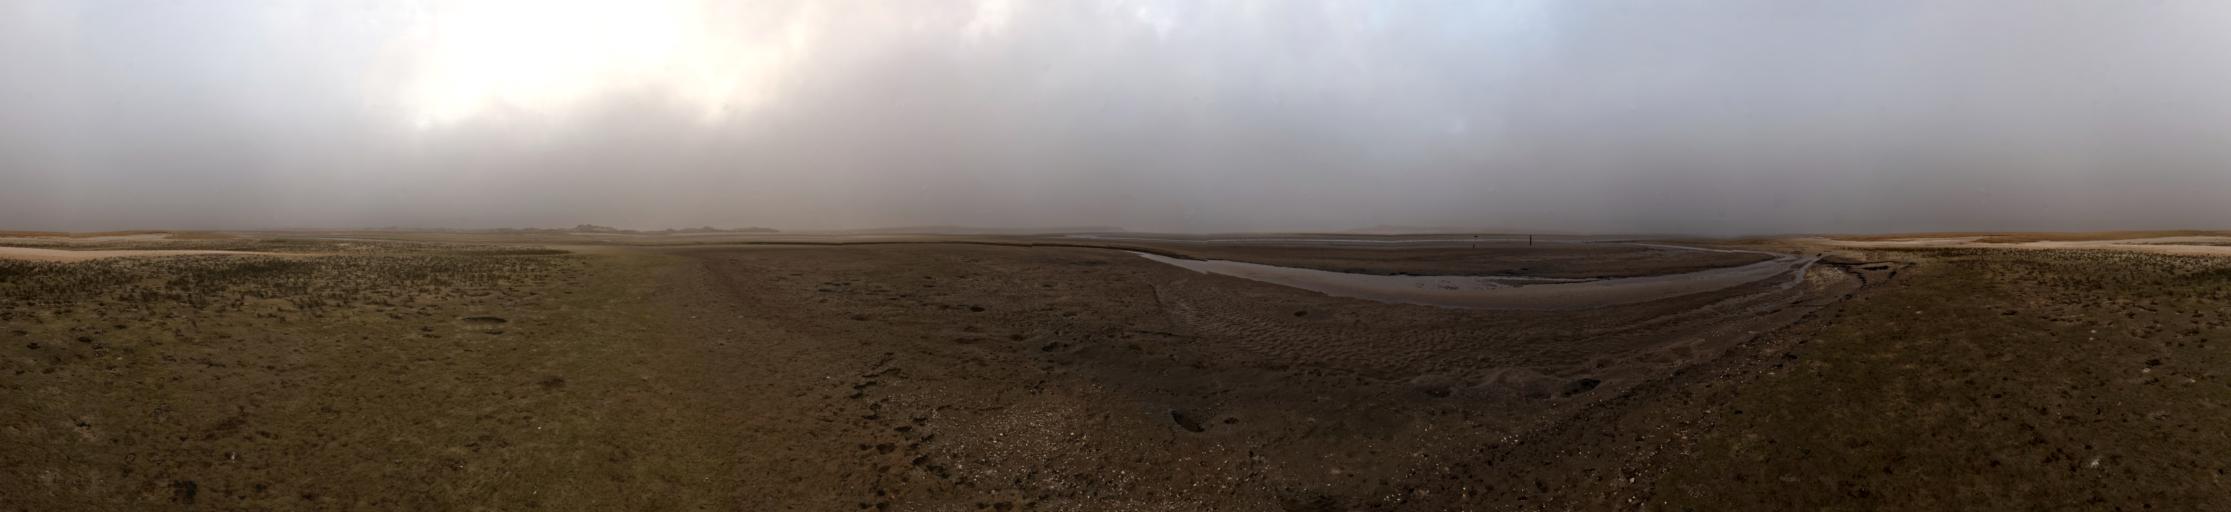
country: NL
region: North Holland
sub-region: Gemeente Texel
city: Den Burg
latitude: 53.1355
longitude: 4.8073
